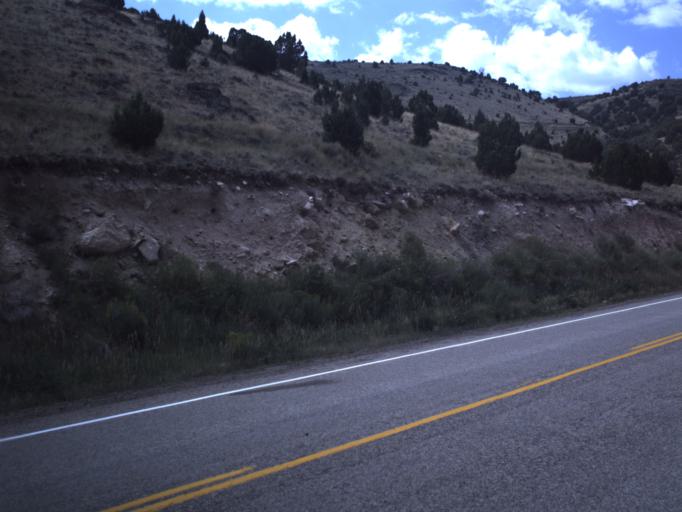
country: US
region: Utah
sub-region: Daggett County
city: Manila
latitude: 40.9096
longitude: -109.6906
